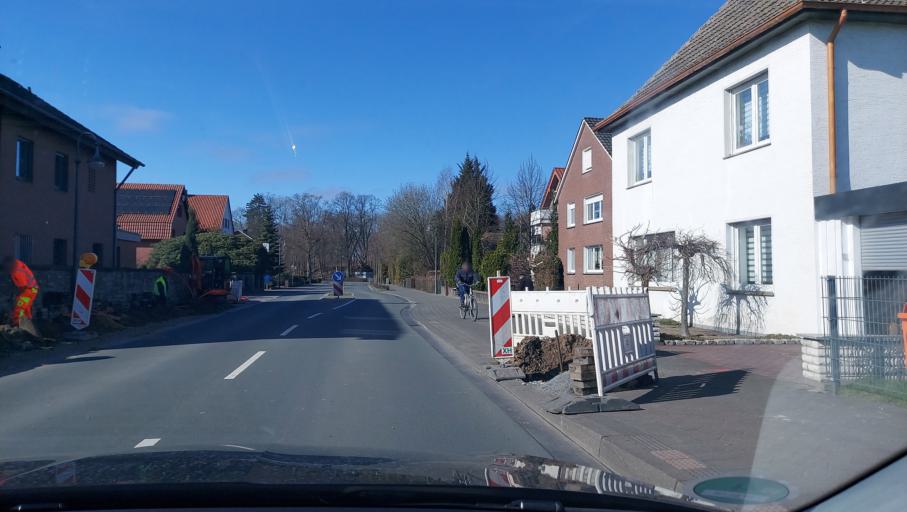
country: DE
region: North Rhine-Westphalia
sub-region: Regierungsbezirk Detmold
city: Guetersloh
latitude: 51.9392
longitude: 8.4418
